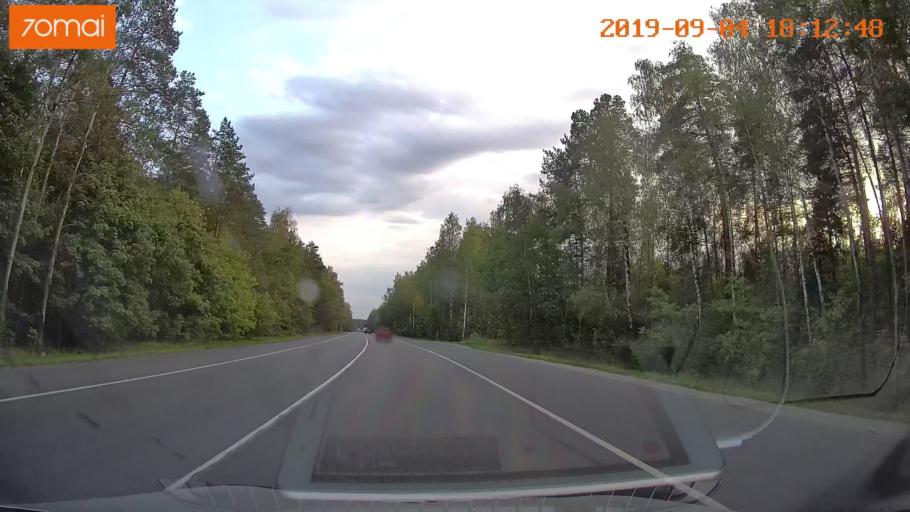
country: RU
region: Moskovskaya
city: Lopatinskiy
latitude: 55.3676
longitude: 38.7373
